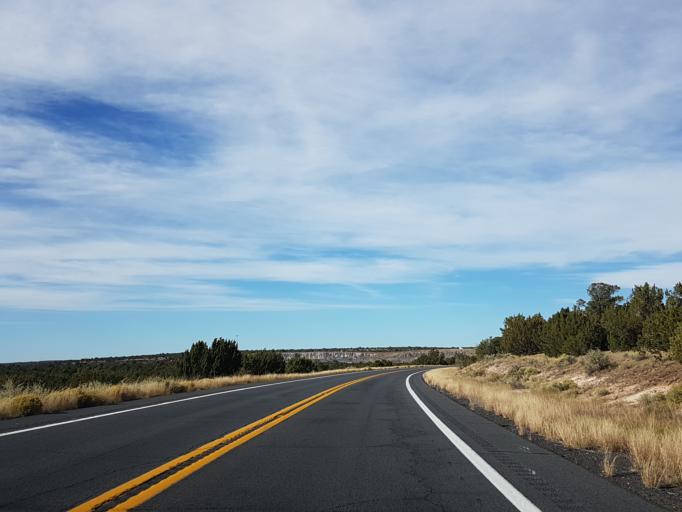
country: US
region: Arizona
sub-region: Coconino County
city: Williams
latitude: 35.4757
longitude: -112.1773
